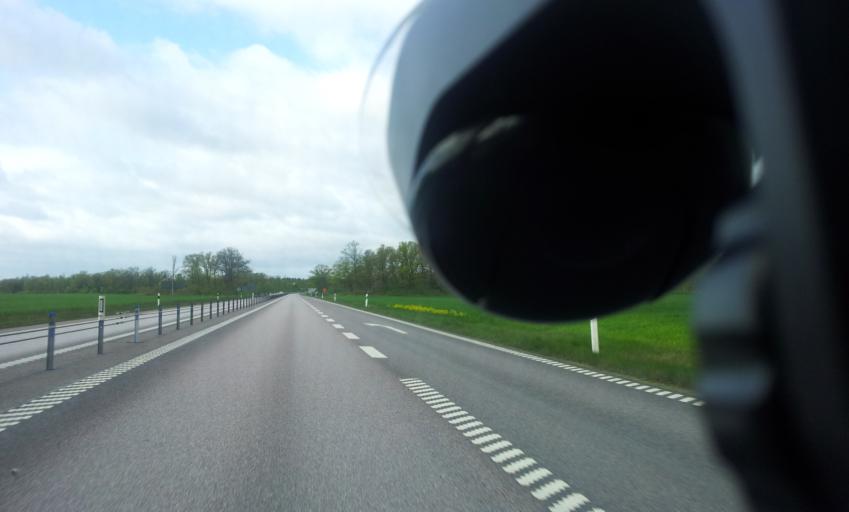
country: SE
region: Kalmar
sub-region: Kalmar Kommun
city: Ljungbyholm
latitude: 56.5873
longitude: 16.1197
